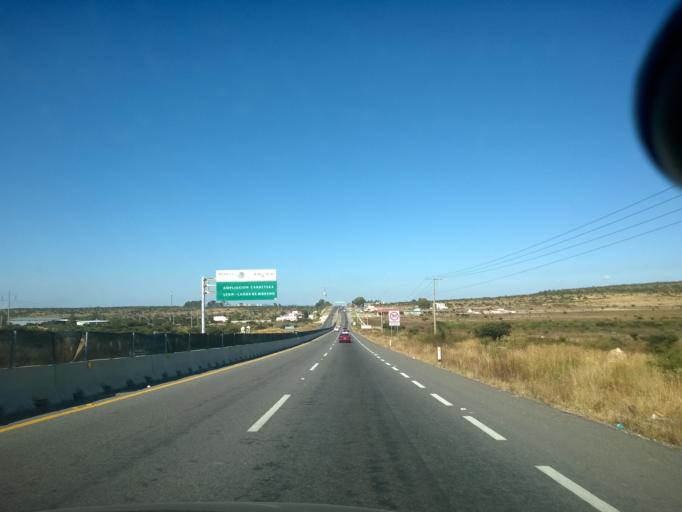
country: MX
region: Jalisco
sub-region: Lagos de Moreno
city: Geovillas Laureles del Campanario
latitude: 21.2831
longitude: -101.8406
